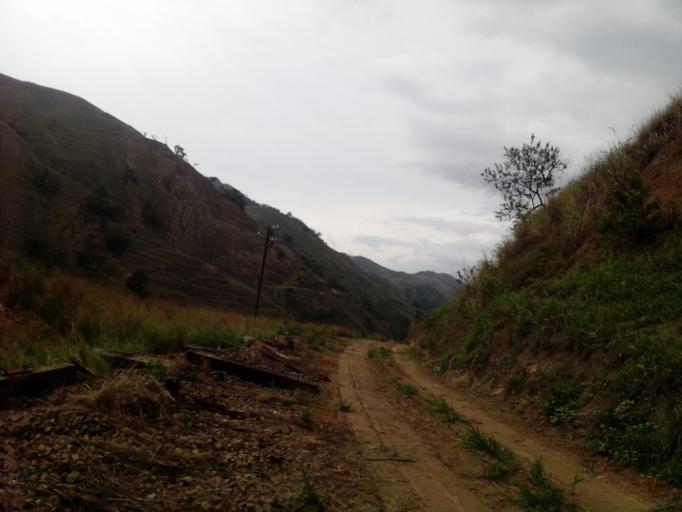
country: BR
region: Rio de Janeiro
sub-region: Miguel Pereira
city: Miguel Pereira
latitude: -22.5029
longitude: -43.5006
